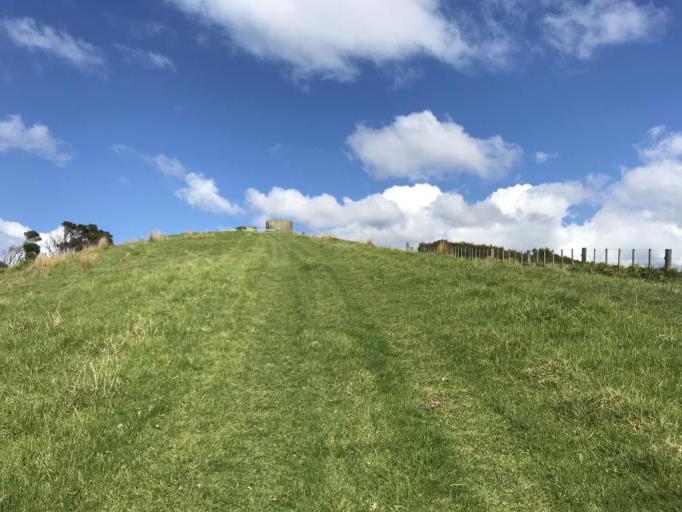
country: NZ
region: Auckland
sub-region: Auckland
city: Warkworth
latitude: -36.3759
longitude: 174.8446
